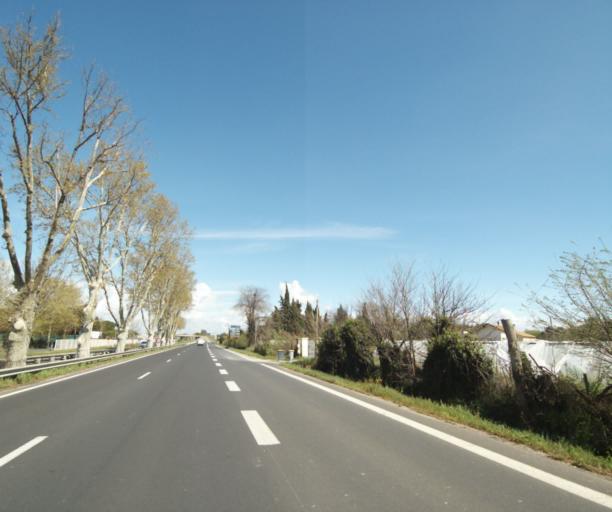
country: FR
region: Languedoc-Roussillon
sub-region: Departement de l'Herault
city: Lattes
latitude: 43.5771
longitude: 3.8976
